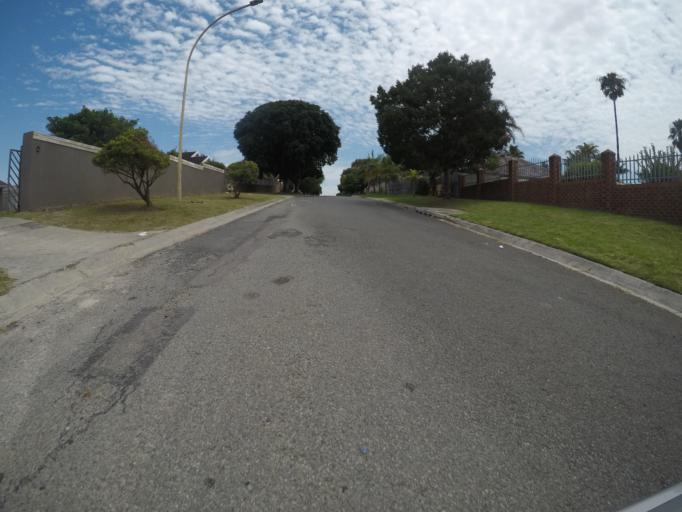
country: ZA
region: Eastern Cape
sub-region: Buffalo City Metropolitan Municipality
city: East London
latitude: -32.9823
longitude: 27.8648
